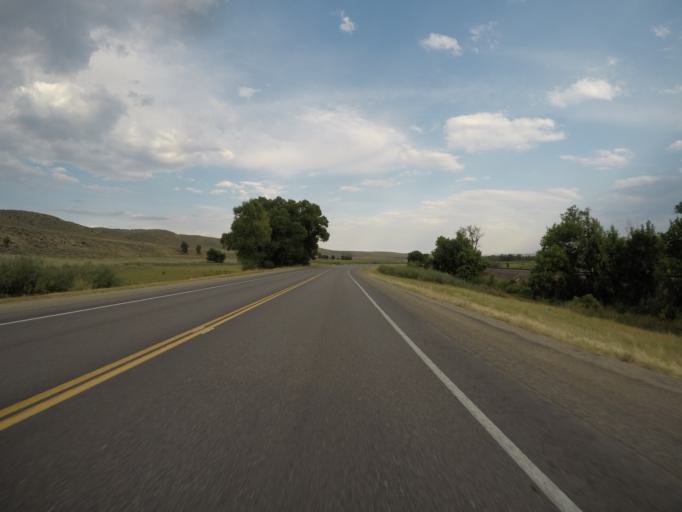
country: US
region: Colorado
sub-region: Moffat County
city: Craig
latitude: 40.5239
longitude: -107.4049
